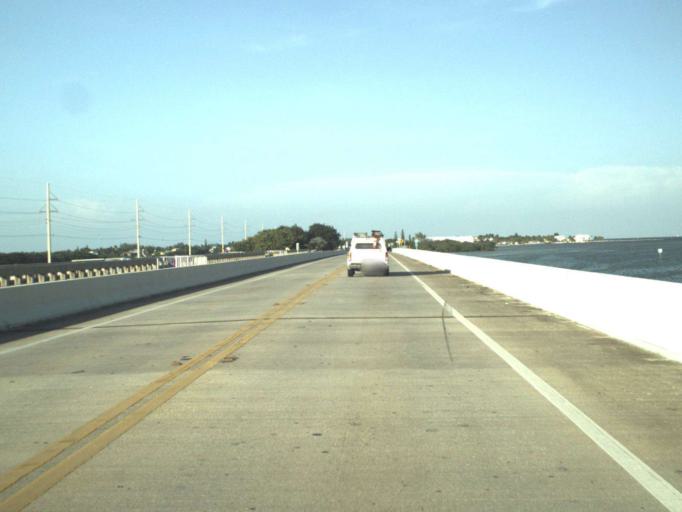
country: US
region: Florida
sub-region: Monroe County
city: Islamorada
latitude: 24.8436
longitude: -80.7498
